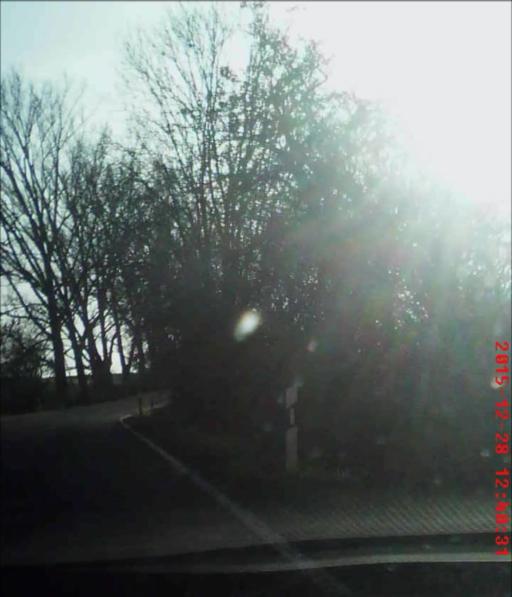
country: DE
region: Thuringia
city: Ossmanstedt
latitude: 51.0096
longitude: 11.4253
